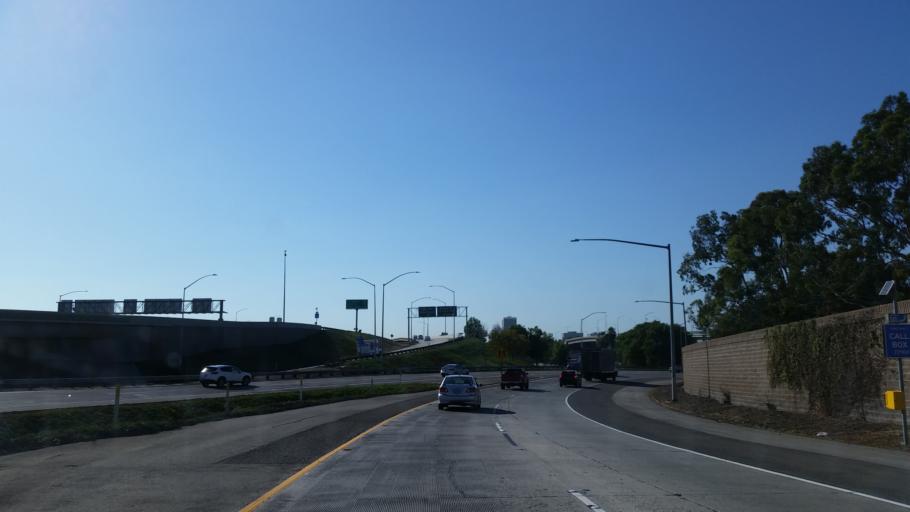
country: US
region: California
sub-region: Orange County
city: Orange
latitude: 33.7794
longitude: -117.8736
